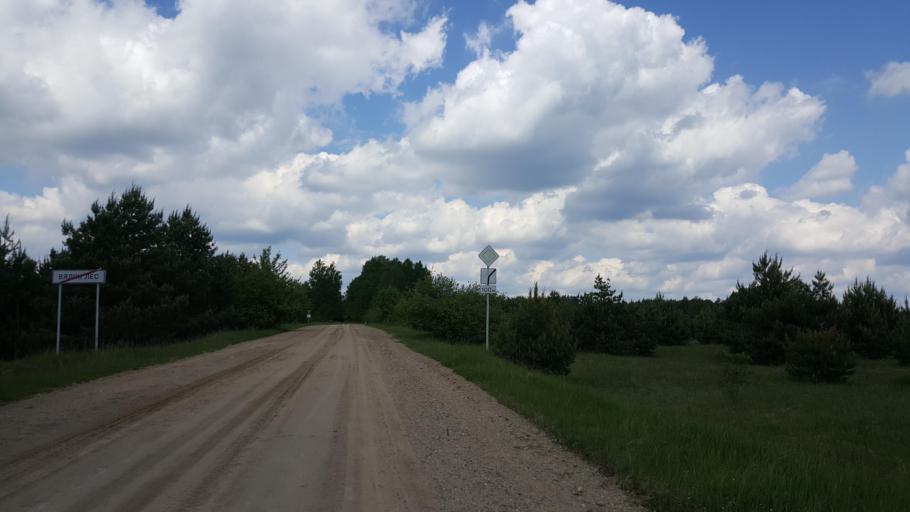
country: BY
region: Brest
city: Kamyanyets
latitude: 52.4805
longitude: 23.9660
